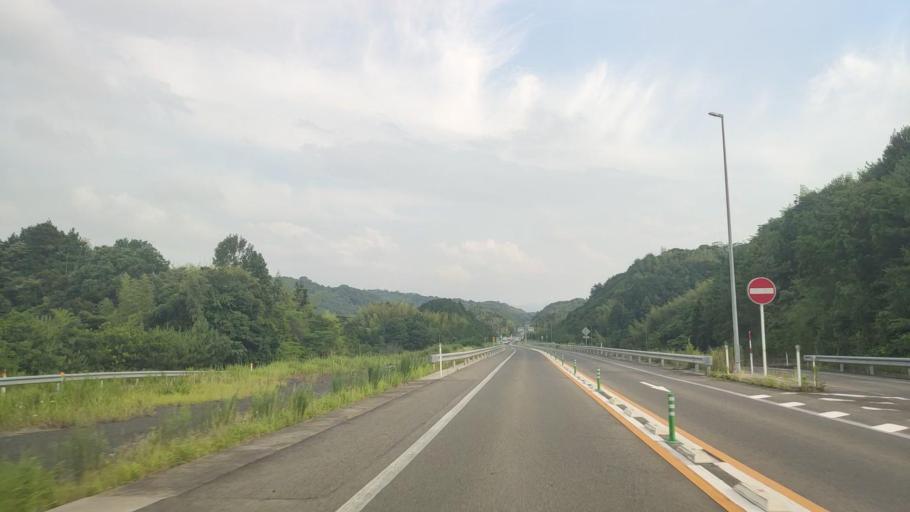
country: JP
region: Tottori
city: Kurayoshi
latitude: 35.4671
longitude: 133.8082
